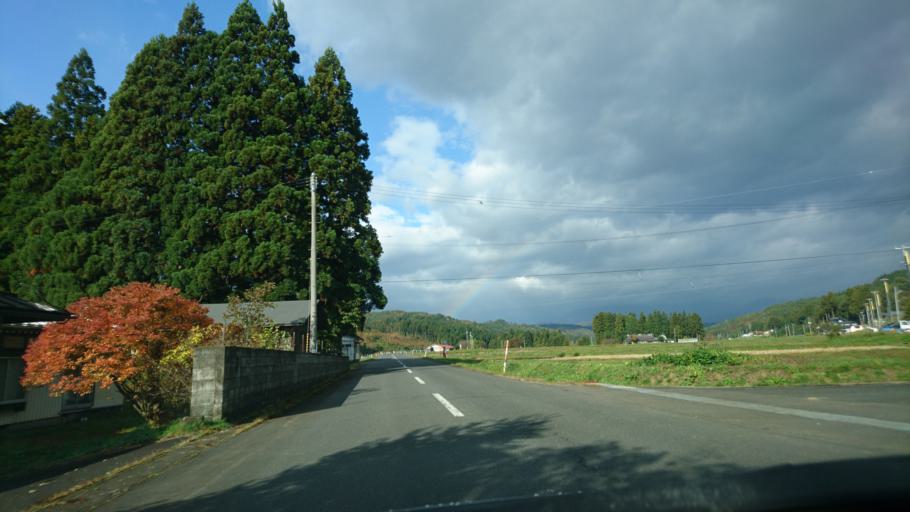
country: JP
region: Iwate
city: Mizusawa
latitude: 39.0759
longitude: 141.0096
